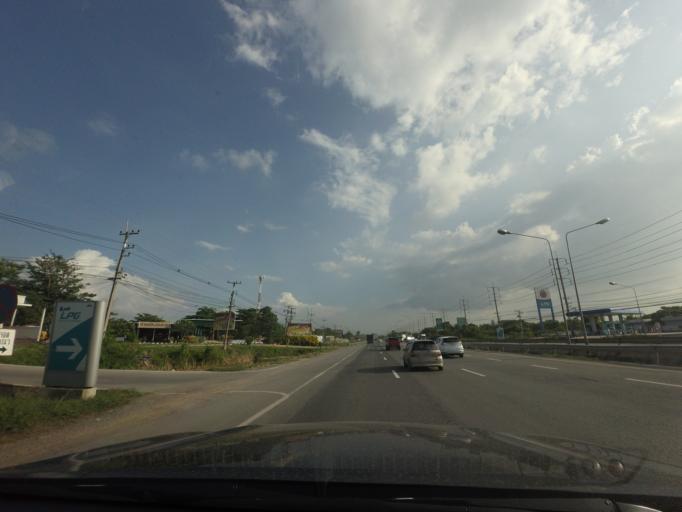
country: TH
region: Sara Buri
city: Chaloem Phra Kiat
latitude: 14.5750
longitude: 100.9020
